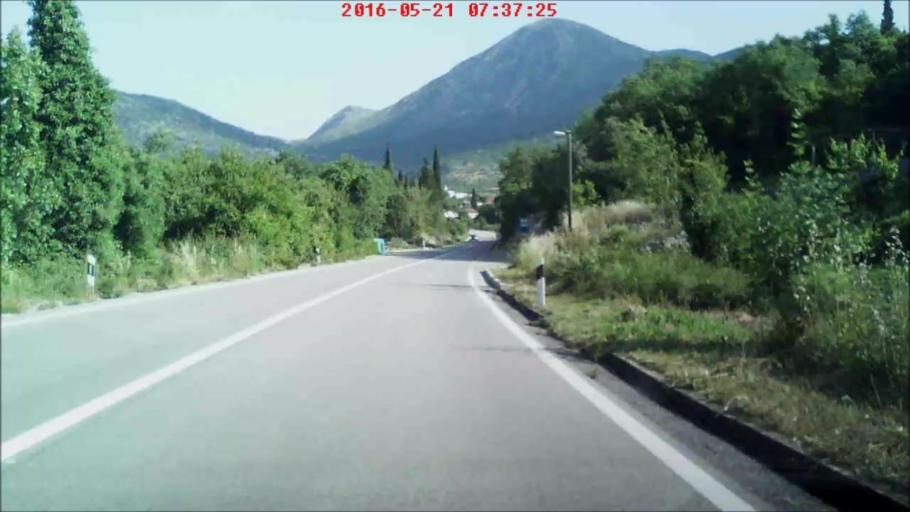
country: HR
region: Dubrovacko-Neretvanska
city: Podgora
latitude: 42.7904
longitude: 17.8542
